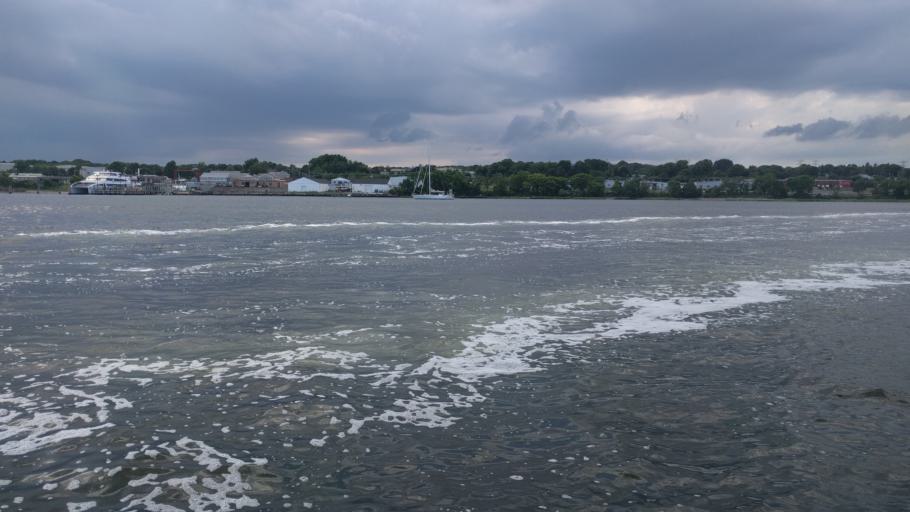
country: US
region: Massachusetts
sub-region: Bristol County
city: Fall River
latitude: 41.7168
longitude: -71.1612
